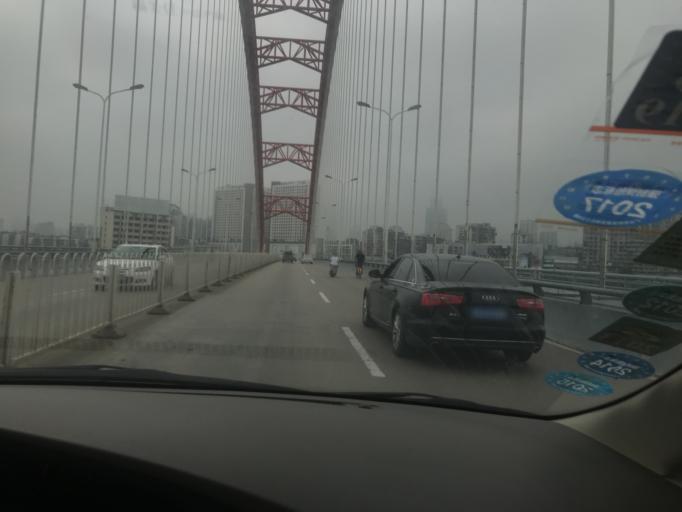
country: CN
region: Hubei
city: Wuhan
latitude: 30.5653
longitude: 114.2797
